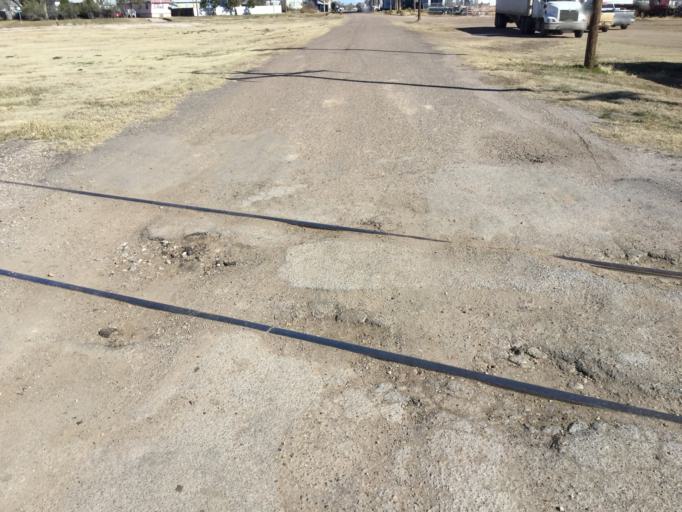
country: US
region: Kansas
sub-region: Morton County
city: Elkhart
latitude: 36.9972
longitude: -101.8987
